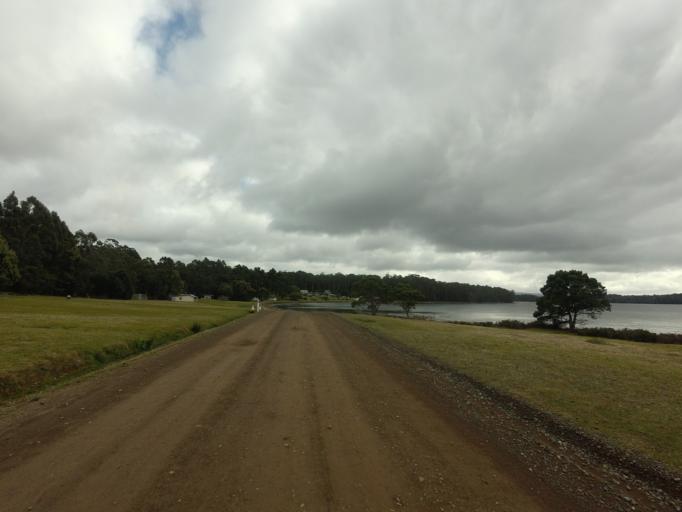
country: AU
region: Tasmania
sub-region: Huon Valley
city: Geeveston
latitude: -43.5373
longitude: 146.8913
